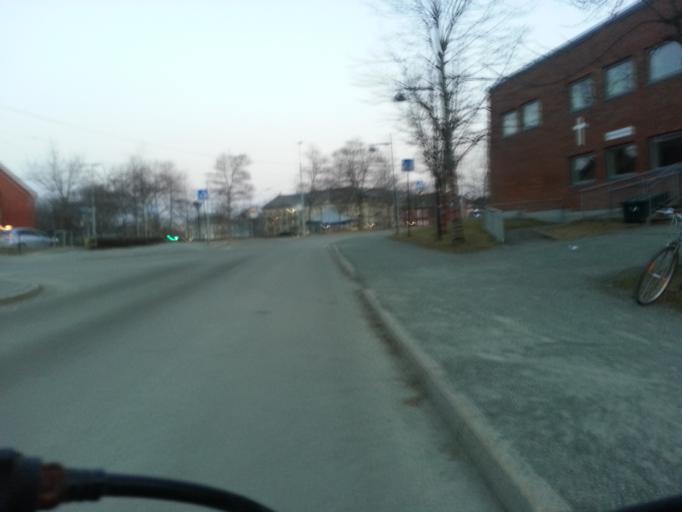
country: NO
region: Sor-Trondelag
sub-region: Trondheim
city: Trondheim
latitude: 63.4292
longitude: 10.3661
